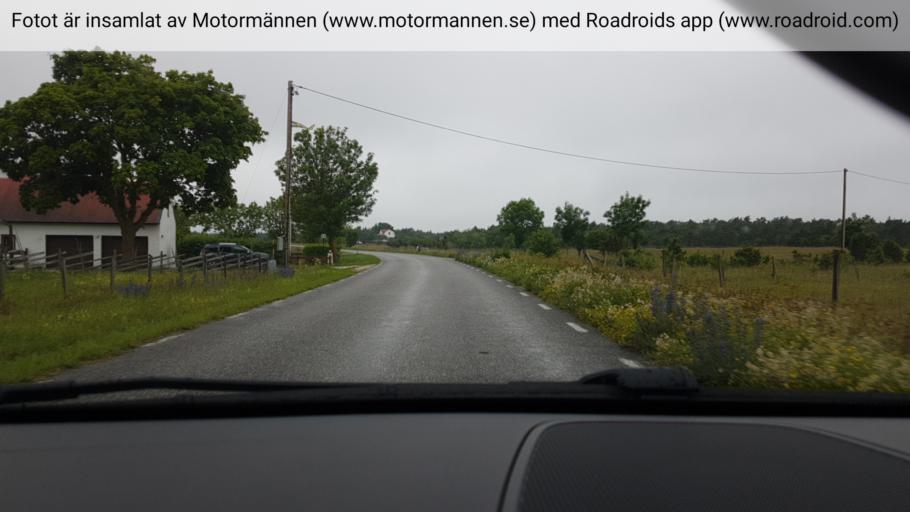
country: SE
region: Gotland
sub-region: Gotland
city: Slite
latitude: 57.8750
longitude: 18.8844
